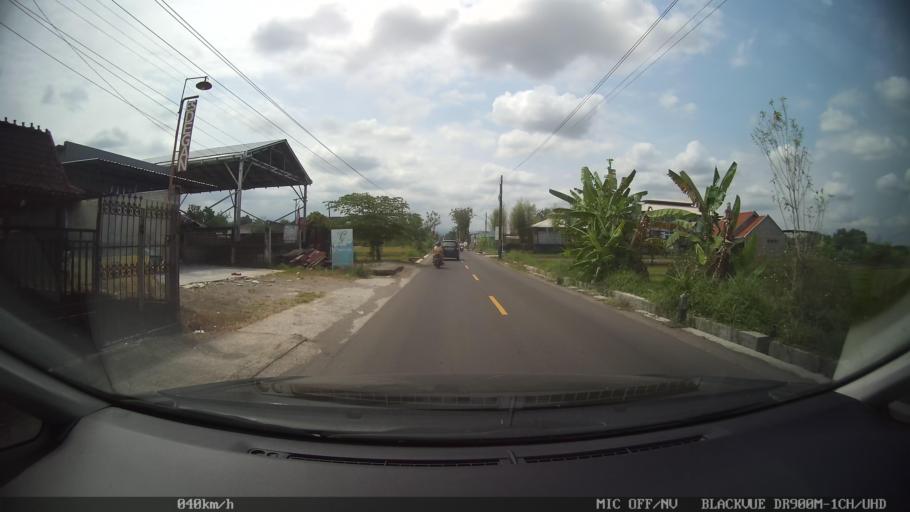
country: ID
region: Central Java
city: Candi Prambanan
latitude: -7.7428
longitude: 110.4814
